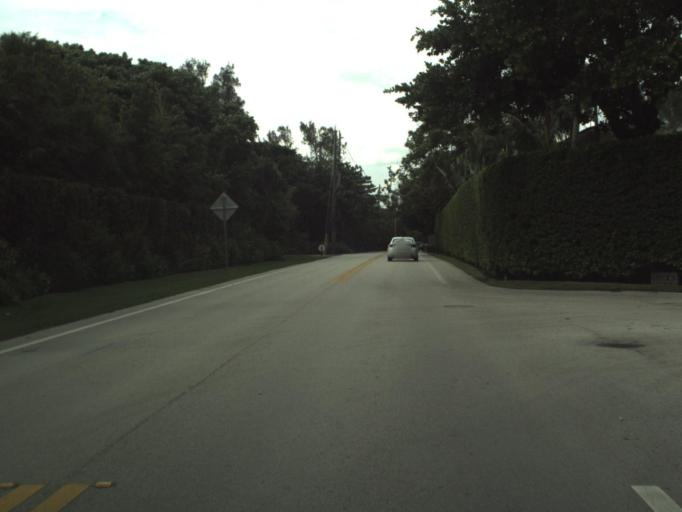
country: US
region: Florida
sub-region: Palm Beach County
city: Palm Beach
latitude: 26.6717
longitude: -80.0382
